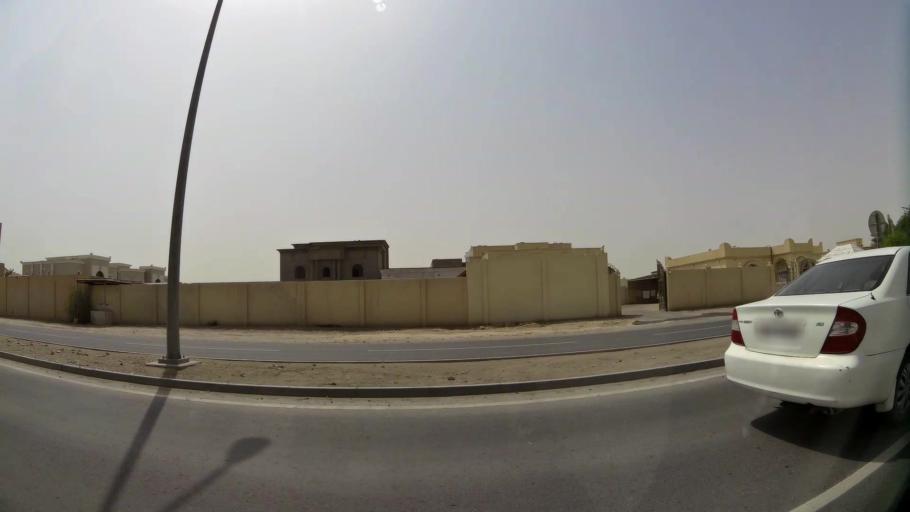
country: QA
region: Baladiyat ar Rayyan
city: Ar Rayyan
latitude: 25.2385
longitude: 51.3814
